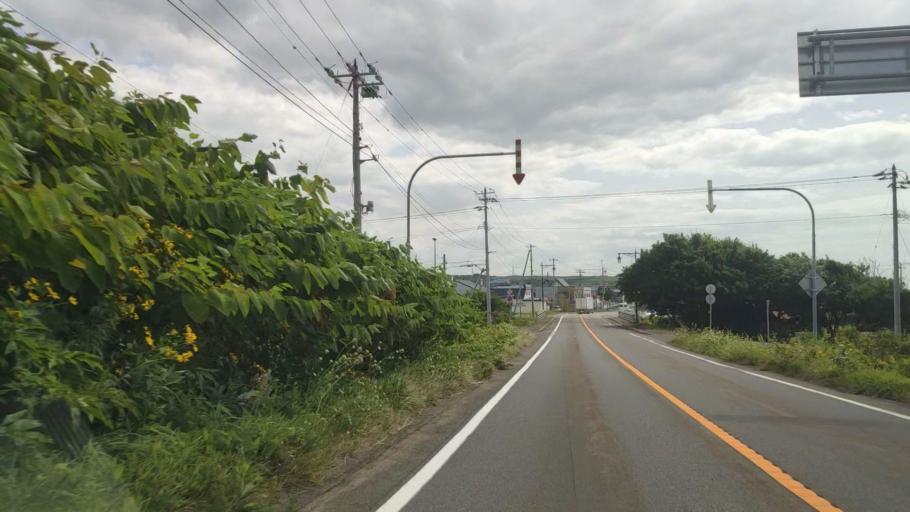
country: JP
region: Hokkaido
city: Rumoi
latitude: 44.5366
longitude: 141.7671
